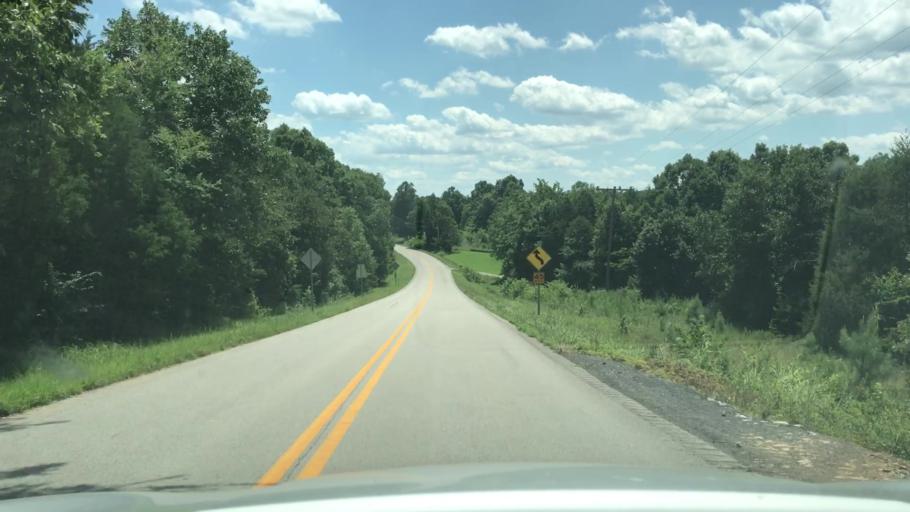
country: US
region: Kentucky
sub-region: Hopkins County
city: Nortonville
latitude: 37.1005
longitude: -87.3405
